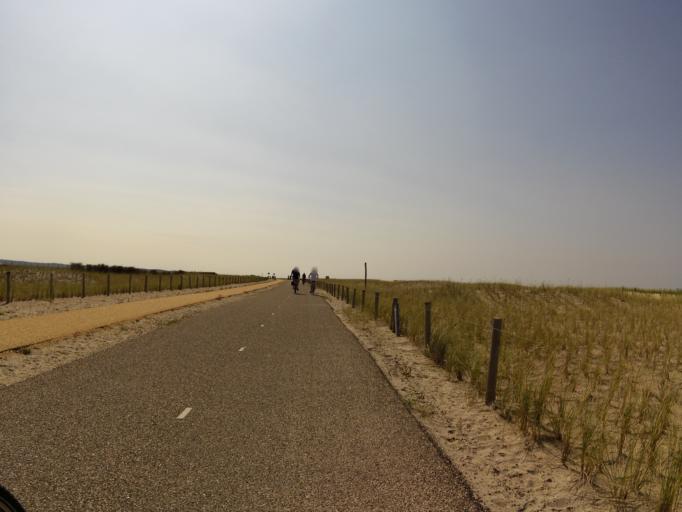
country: NL
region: North Holland
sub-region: Gemeente Schagen
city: Harenkarspel
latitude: 52.7683
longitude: 4.6548
